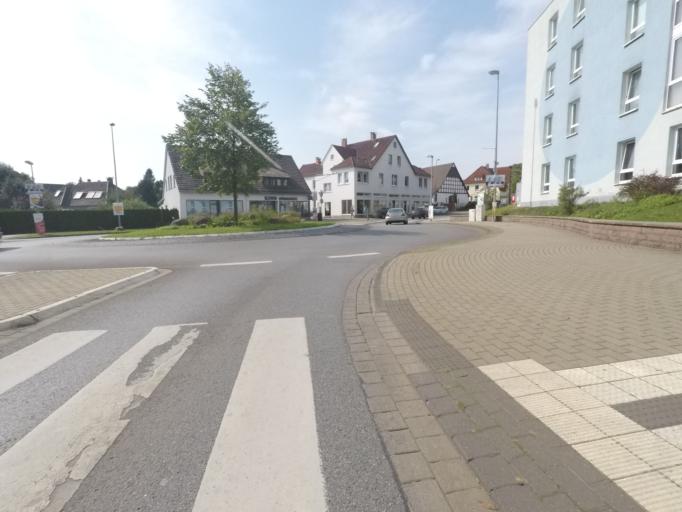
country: DE
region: North Rhine-Westphalia
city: Spenge
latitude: 52.0965
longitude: 8.5210
